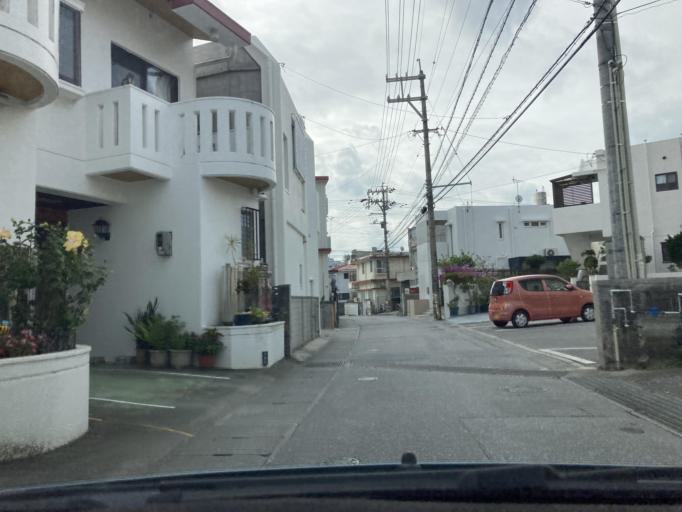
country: JP
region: Okinawa
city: Ginowan
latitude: 26.2041
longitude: 127.7528
